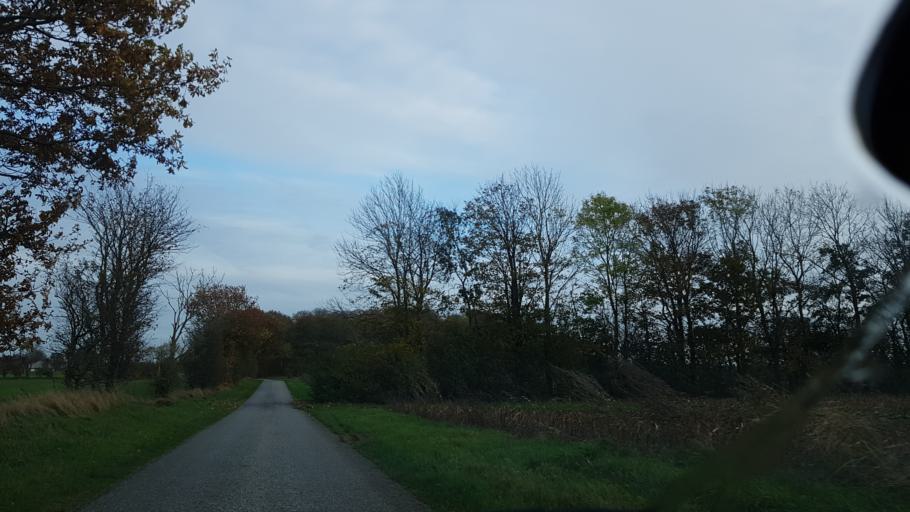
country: DK
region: South Denmark
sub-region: Haderslev Kommune
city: Vojens
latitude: 55.2986
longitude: 9.2642
